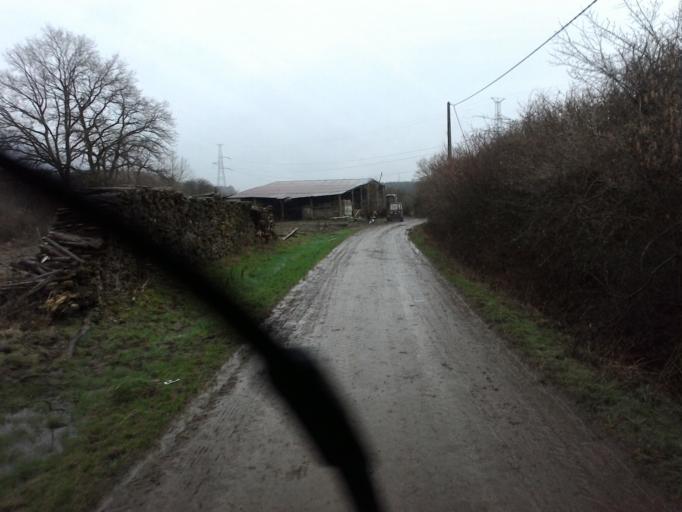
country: BE
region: Wallonia
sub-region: Province de Namur
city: Gedinne
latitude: 50.0250
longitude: 4.8499
